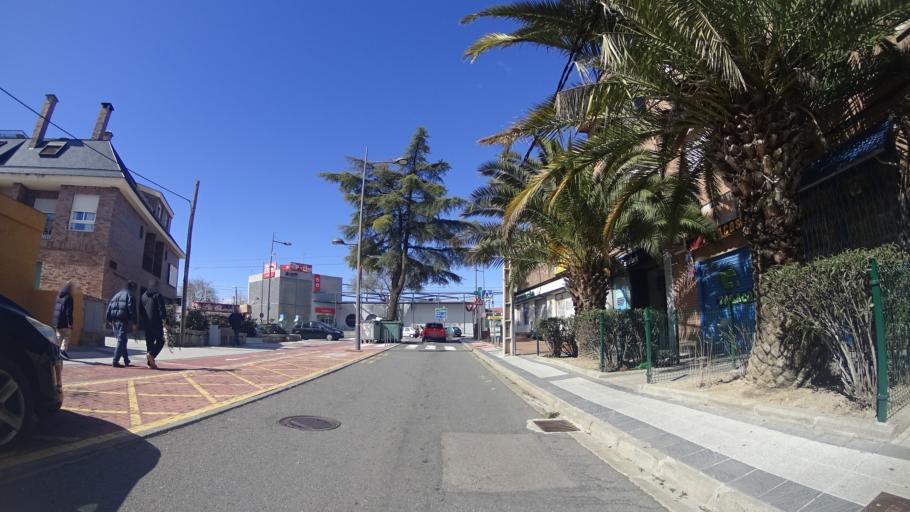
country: ES
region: Madrid
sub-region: Provincia de Madrid
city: Las Matas
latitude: 40.5526
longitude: -3.8959
